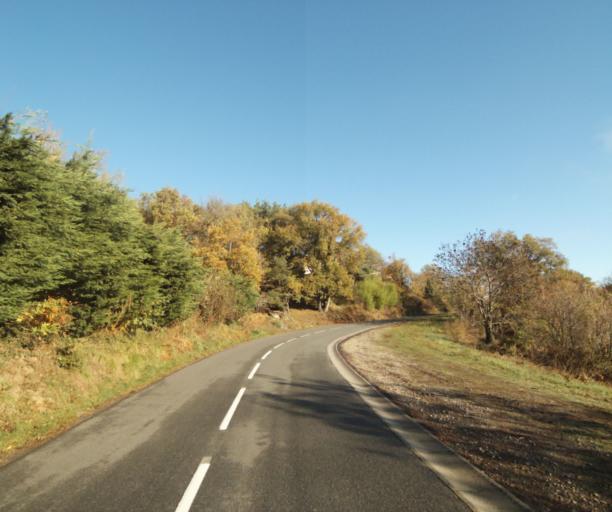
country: FR
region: Auvergne
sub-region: Departement du Puy-de-Dome
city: Nohanent
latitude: 45.8126
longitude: 3.0373
